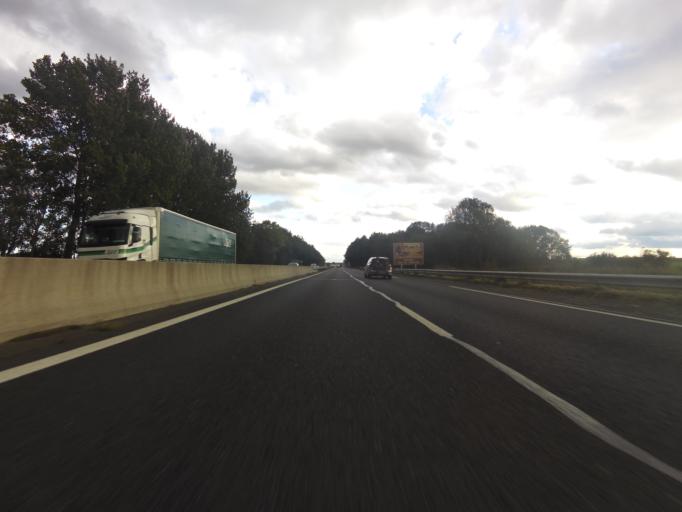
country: FR
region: Haute-Normandie
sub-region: Departement de la Seine-Maritime
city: Saint-Martin-Osmonville
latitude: 49.6031
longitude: 1.2709
